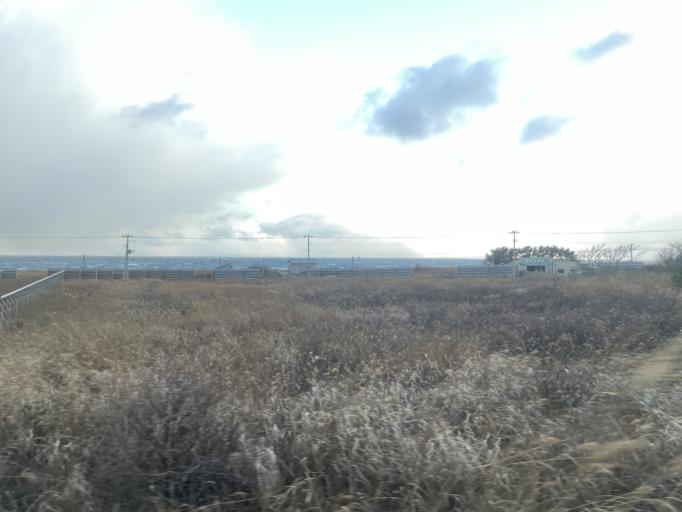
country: JP
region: Aomori
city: Mutsu
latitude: 41.0960
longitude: 141.2511
